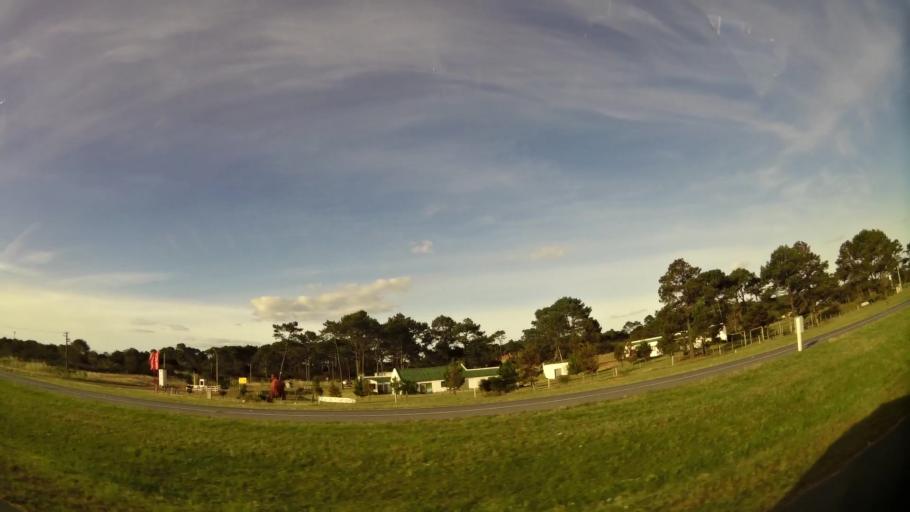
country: UY
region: Maldonado
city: Maldonado
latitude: -34.8737
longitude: -55.0745
